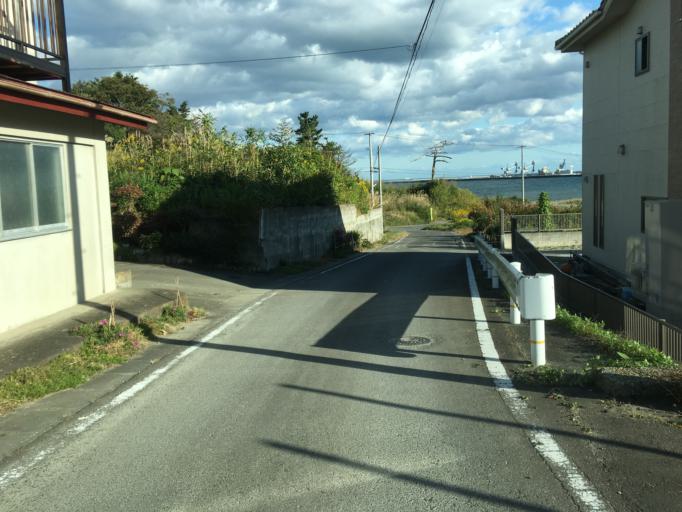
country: JP
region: Miyagi
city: Marumori
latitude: 37.8668
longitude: 140.9379
